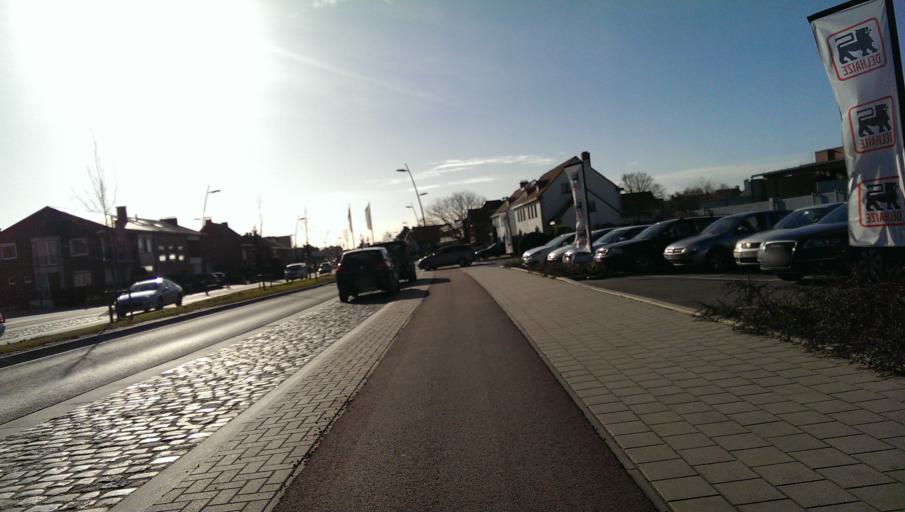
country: BE
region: Flanders
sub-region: Provincie West-Vlaanderen
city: Roeselare
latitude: 50.9415
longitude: 3.1145
